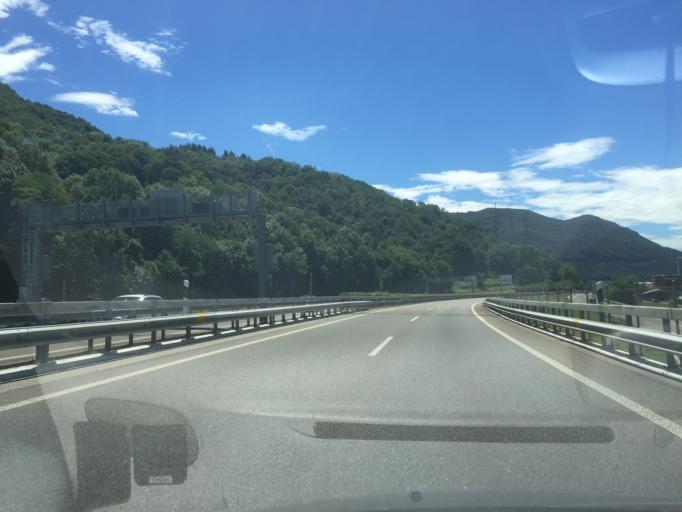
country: CH
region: Ticino
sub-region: Lugano District
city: Sorengo
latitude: 45.9837
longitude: 8.9330
